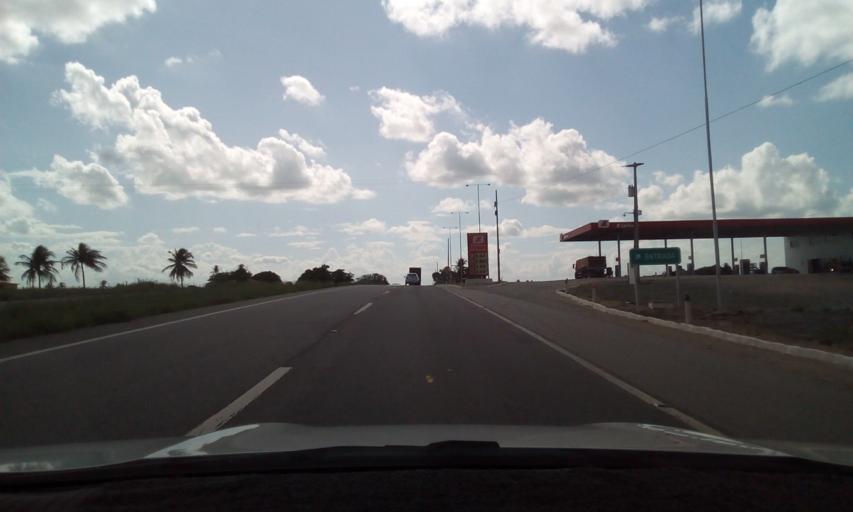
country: BR
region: Paraiba
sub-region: Pilar
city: Pilar
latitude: -7.1901
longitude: -35.2731
